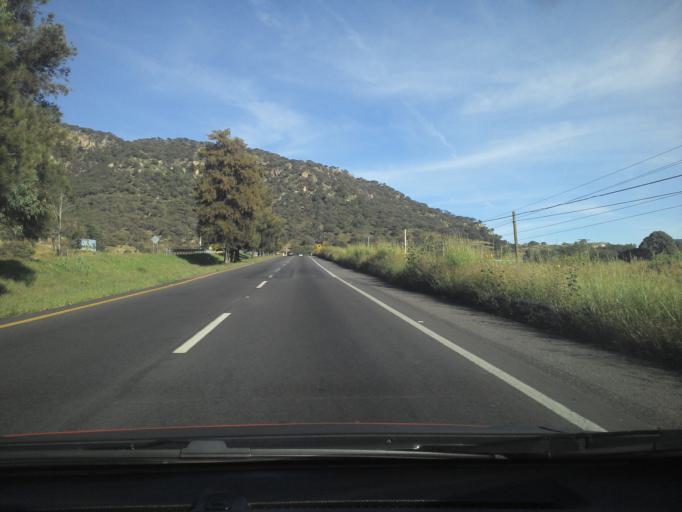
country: MX
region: Jalisco
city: La Venta del Astillero
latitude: 20.7364
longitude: -103.5831
